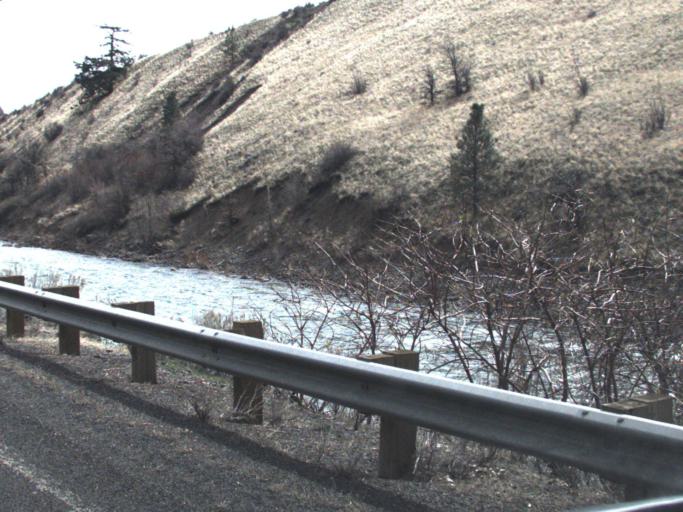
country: US
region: Washington
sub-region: Yakima County
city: Tieton
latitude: 46.7667
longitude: -120.8328
